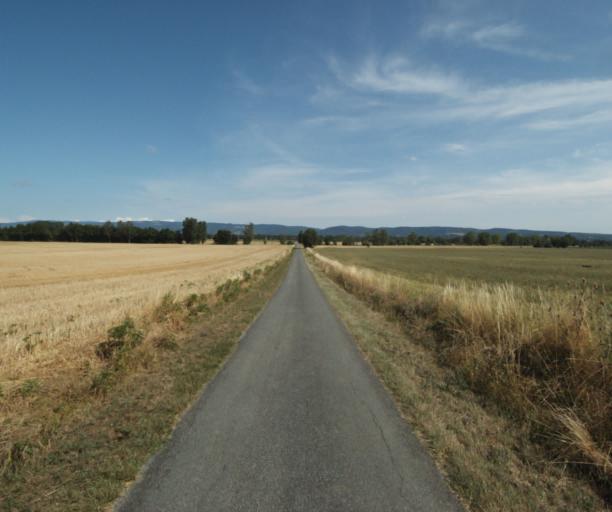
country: FR
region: Midi-Pyrenees
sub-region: Departement de la Haute-Garonne
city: Revel
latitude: 43.4997
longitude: 1.9798
